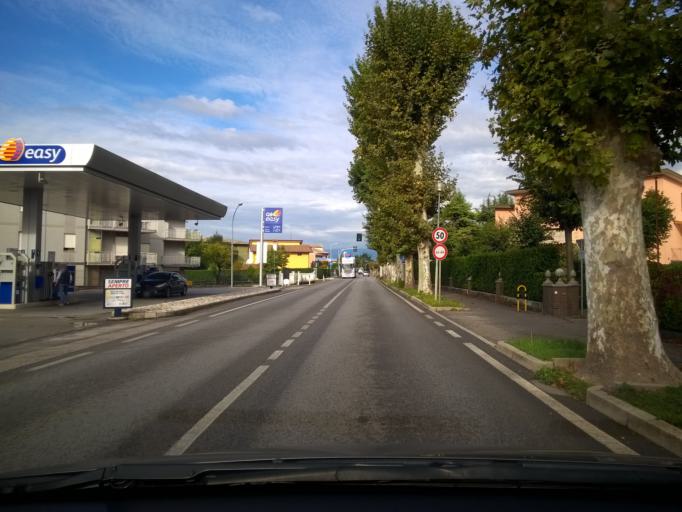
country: IT
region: Veneto
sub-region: Provincia di Treviso
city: Castello di Godego
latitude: 45.6885
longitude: 11.8842
